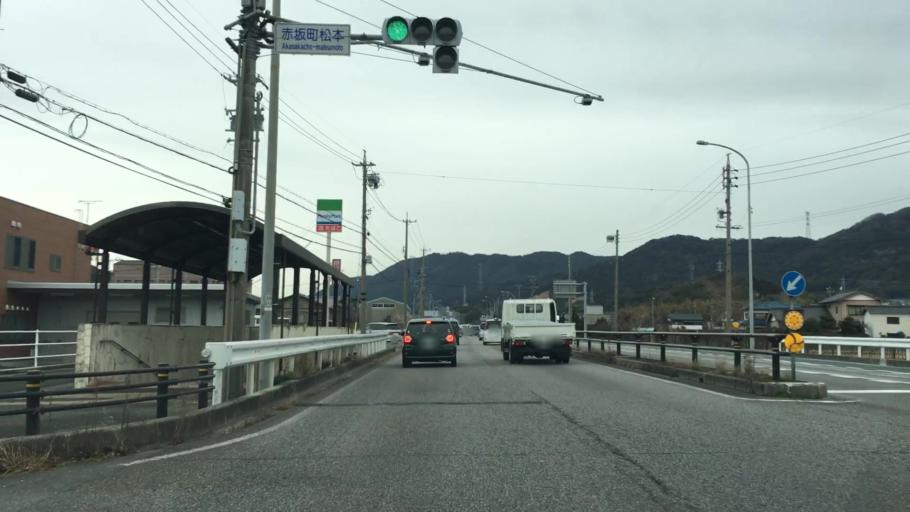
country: JP
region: Aichi
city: Kozakai-cho
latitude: 34.8576
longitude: 137.3103
